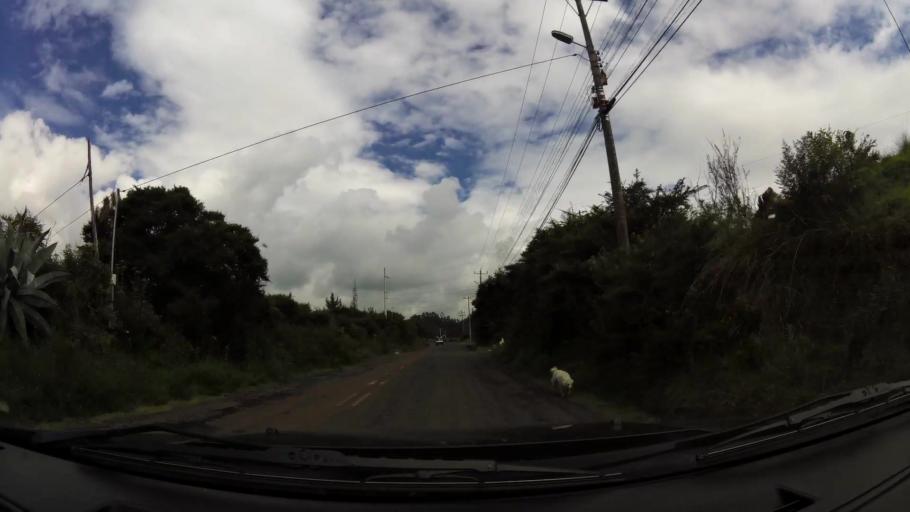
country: EC
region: Pichincha
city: Sangolqui
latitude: -0.3235
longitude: -78.3976
